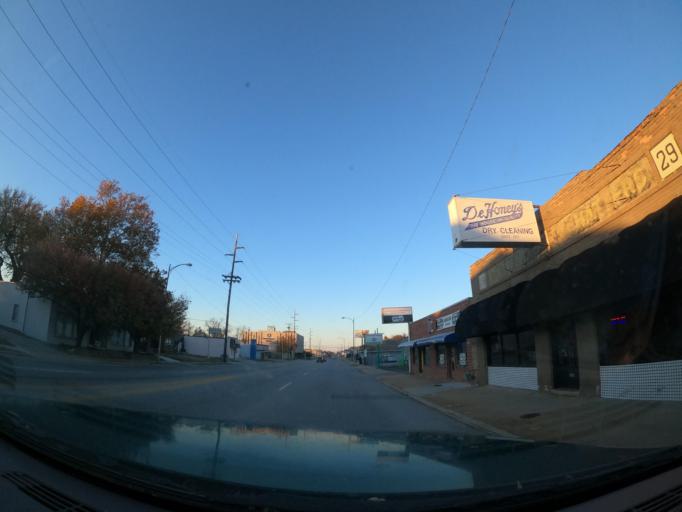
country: US
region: Oklahoma
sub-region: Tulsa County
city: Tulsa
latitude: 36.1414
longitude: -95.9403
